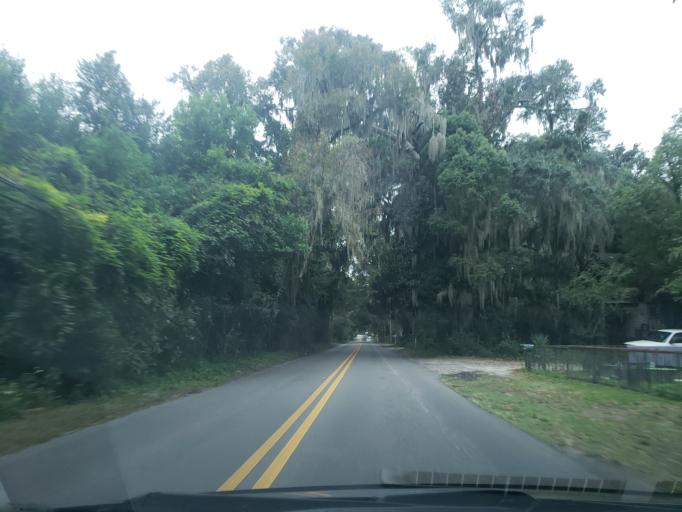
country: US
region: Georgia
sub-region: Chatham County
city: Montgomery
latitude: 31.9608
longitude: -81.1021
